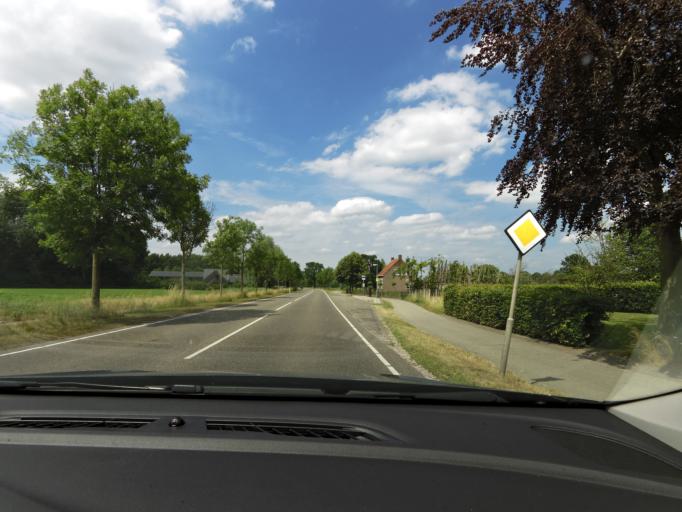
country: NL
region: North Brabant
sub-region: Gemeente Baarle-Nassau
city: Baarle-Nassau
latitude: 51.4940
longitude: 4.8748
